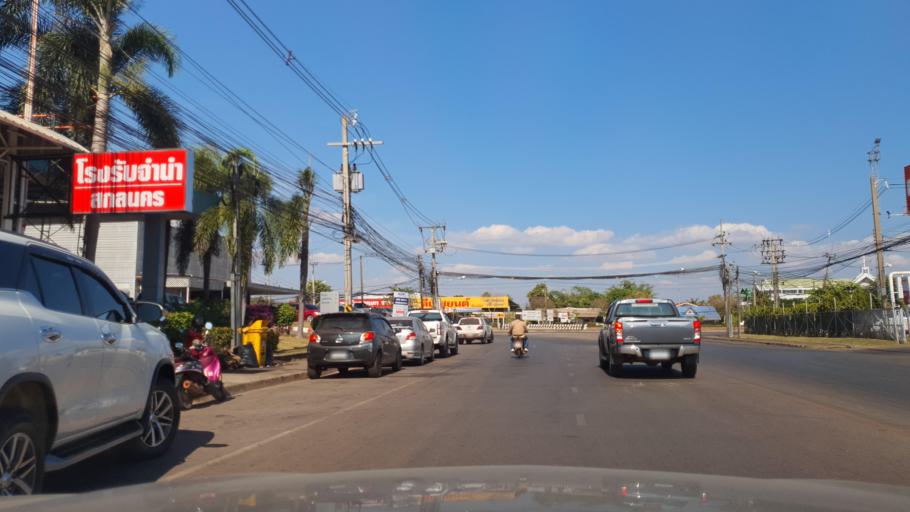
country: TH
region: Sakon Nakhon
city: Sakon Nakhon
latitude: 17.1745
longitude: 104.1278
